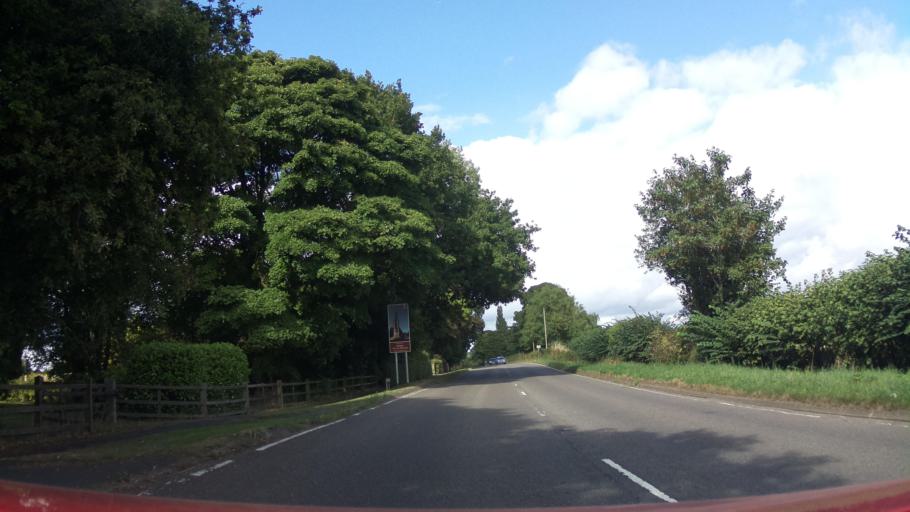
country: GB
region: England
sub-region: Leicestershire
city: Ashby de la Zouch
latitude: 52.7319
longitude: -1.4859
